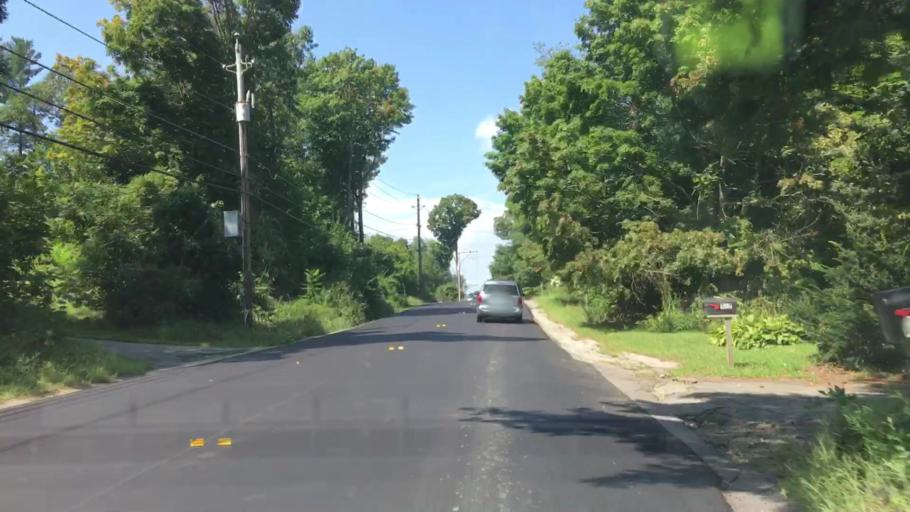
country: US
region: New Hampshire
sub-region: Rockingham County
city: Hampstead
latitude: 42.8932
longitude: -71.2083
